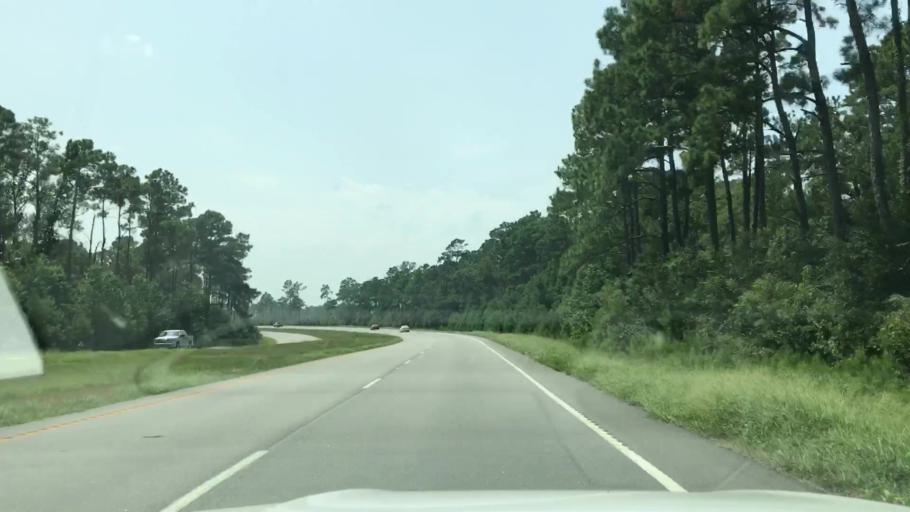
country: US
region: South Carolina
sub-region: Georgetown County
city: Georgetown
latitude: 33.1812
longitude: -79.4105
